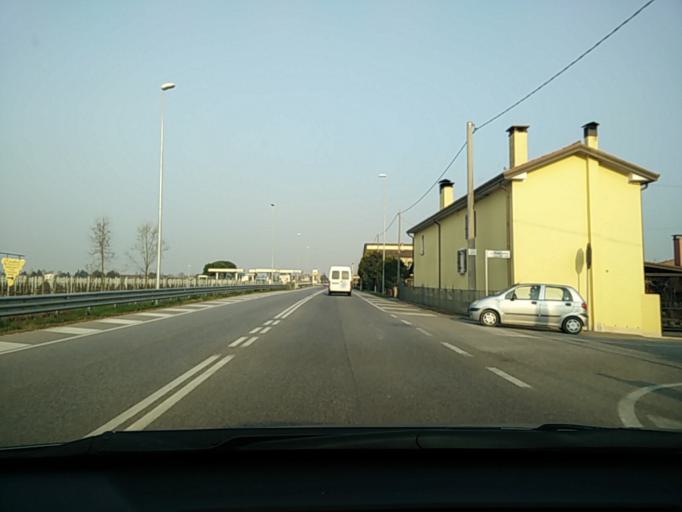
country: IT
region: Veneto
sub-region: Provincia di Treviso
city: Ponzano
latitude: 45.7313
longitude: 12.2294
